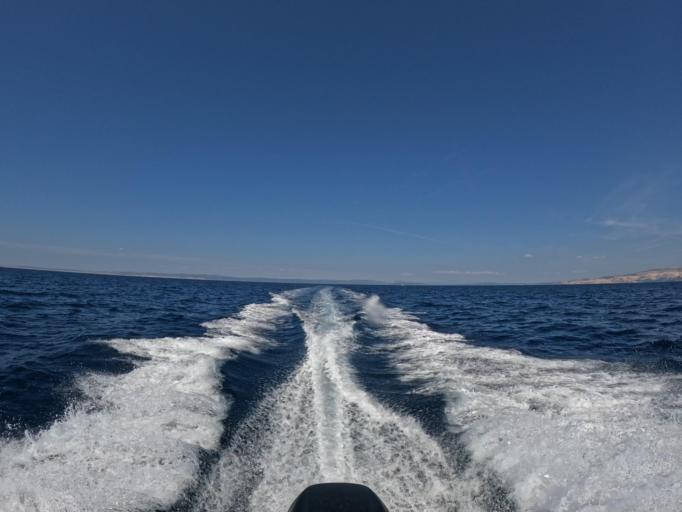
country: HR
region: Primorsko-Goranska
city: Lopar
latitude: 44.8626
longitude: 14.6868
